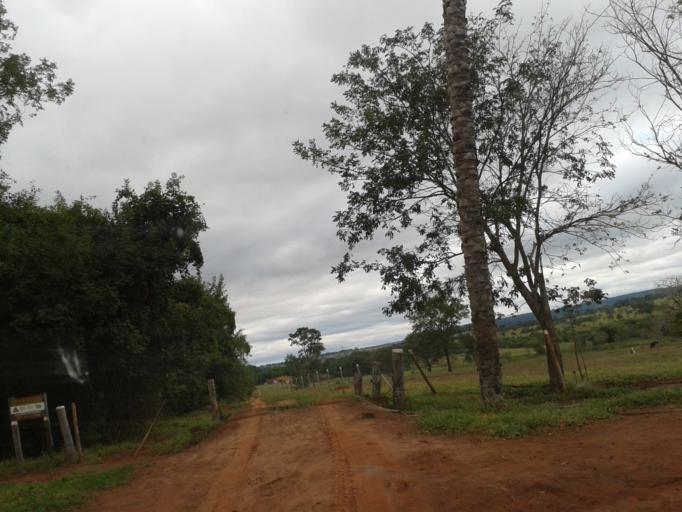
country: BR
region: Minas Gerais
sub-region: Campina Verde
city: Campina Verde
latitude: -19.4841
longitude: -49.6164
